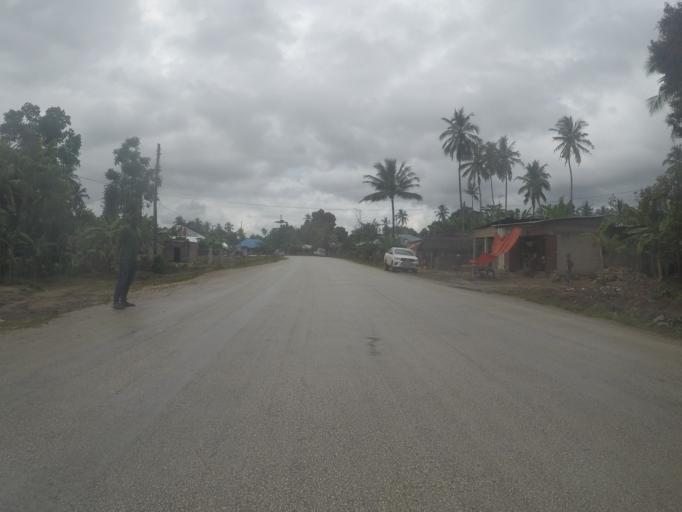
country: TZ
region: Zanzibar North
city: Gamba
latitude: -6.0021
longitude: 39.2521
